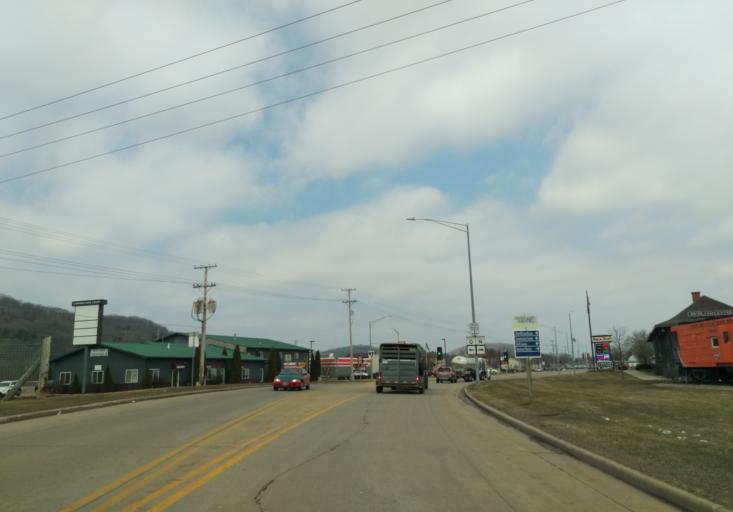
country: US
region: Wisconsin
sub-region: Richland County
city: Richland Center
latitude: 43.3338
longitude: -90.3888
